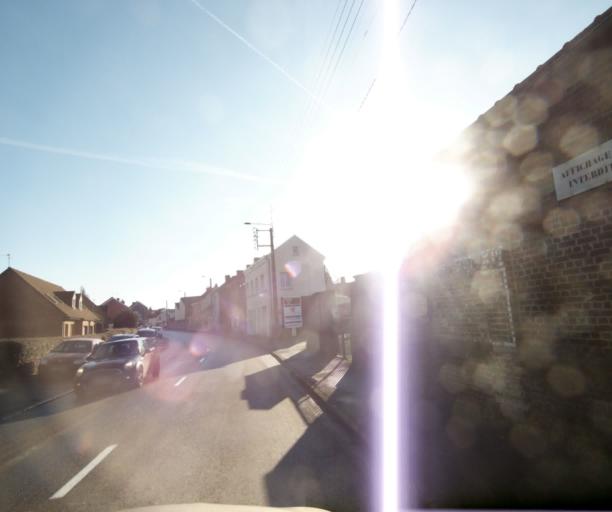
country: FR
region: Nord-Pas-de-Calais
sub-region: Departement du Nord
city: Marly
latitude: 50.3459
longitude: 3.5436
